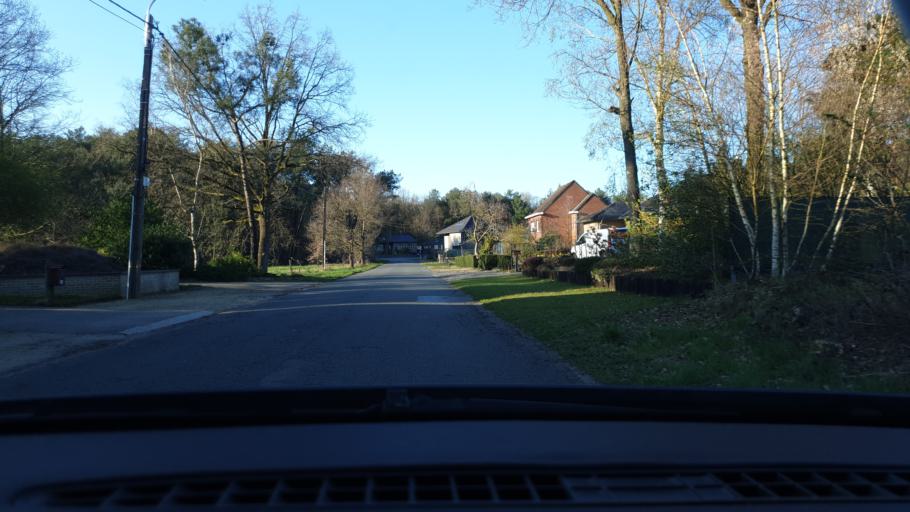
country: BE
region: Flanders
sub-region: Provincie Antwerpen
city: Geel
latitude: 51.1340
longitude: 5.0073
